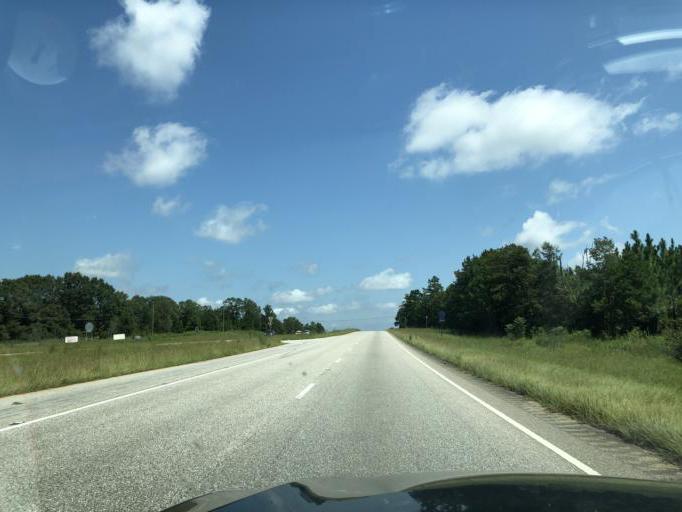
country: US
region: Alabama
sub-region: Henry County
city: Abbeville
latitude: 31.7197
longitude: -85.2681
